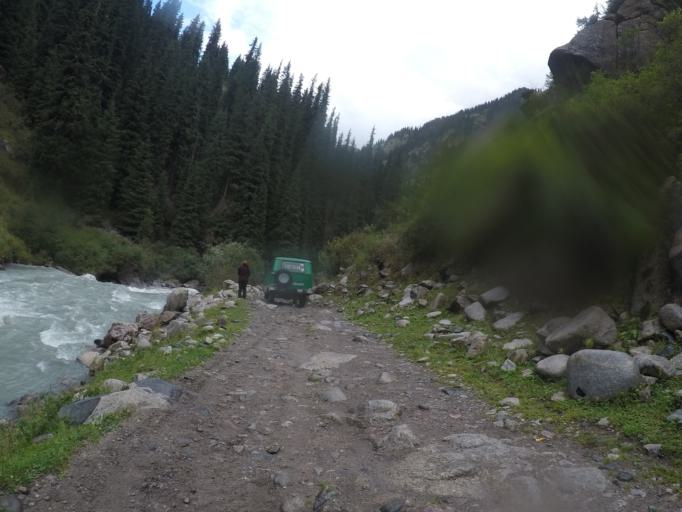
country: KG
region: Ysyk-Koel
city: Teploklyuchenka
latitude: 42.4154
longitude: 78.5713
